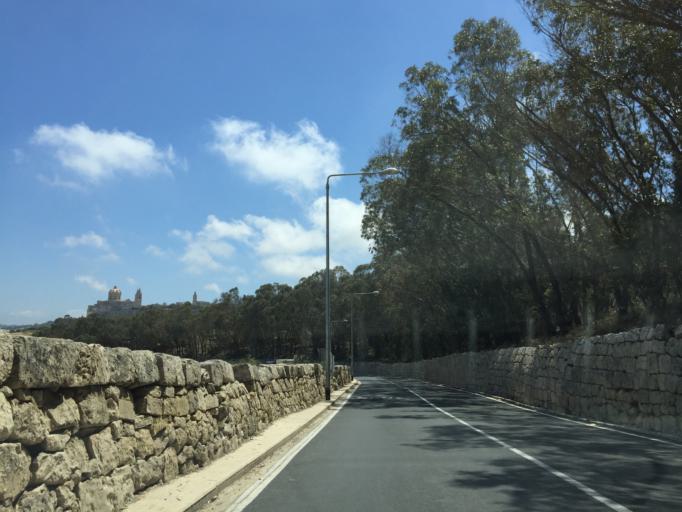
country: MT
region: L-Imtarfa
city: Imtarfa
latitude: 35.8945
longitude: 14.4033
